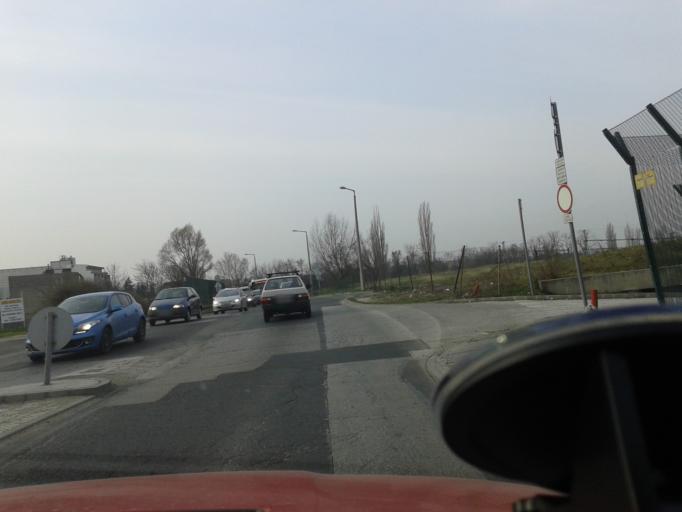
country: HU
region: Budapest
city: Budapest XI. keruelet
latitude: 47.4584
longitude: 19.0234
